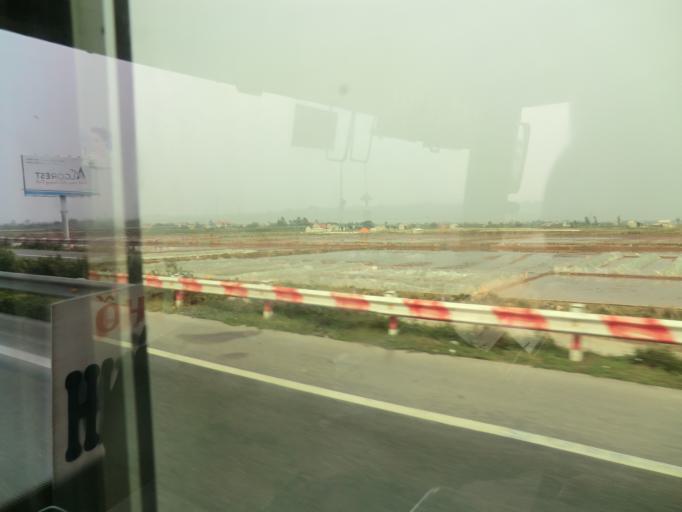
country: VN
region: Ha Noi
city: Thuong Tin
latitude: 20.8392
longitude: 105.8867
